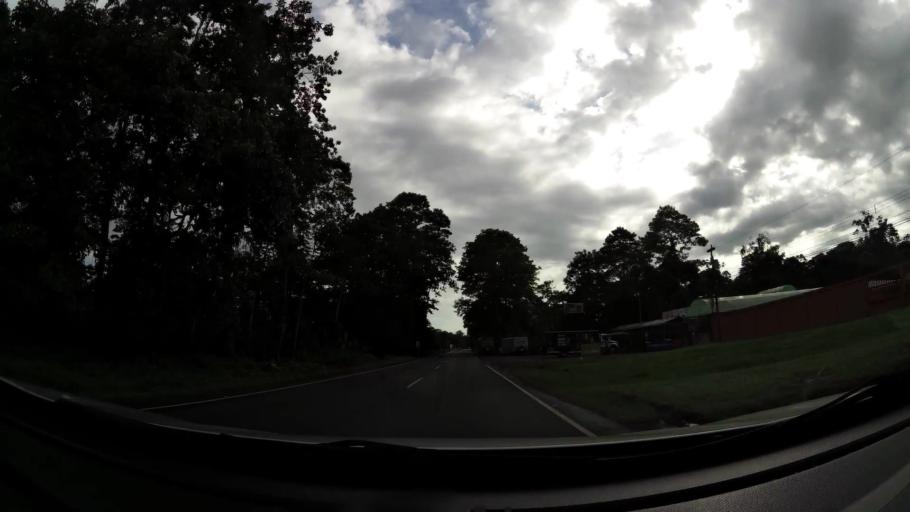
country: CR
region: Limon
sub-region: Canton de Guacimo
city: Guacimo
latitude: 10.2055
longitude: -83.7365
